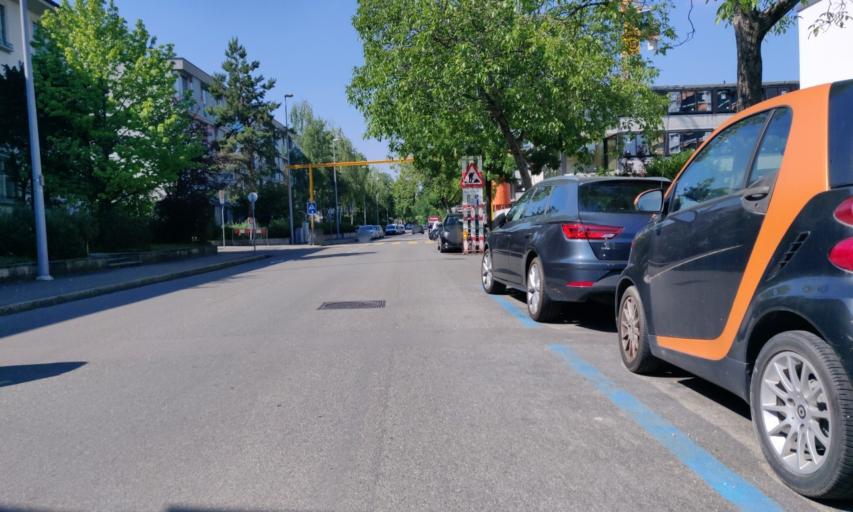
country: CH
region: Basel-Landschaft
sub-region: Bezirk Arlesheim
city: Birsfelden
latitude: 47.5457
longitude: 7.6188
